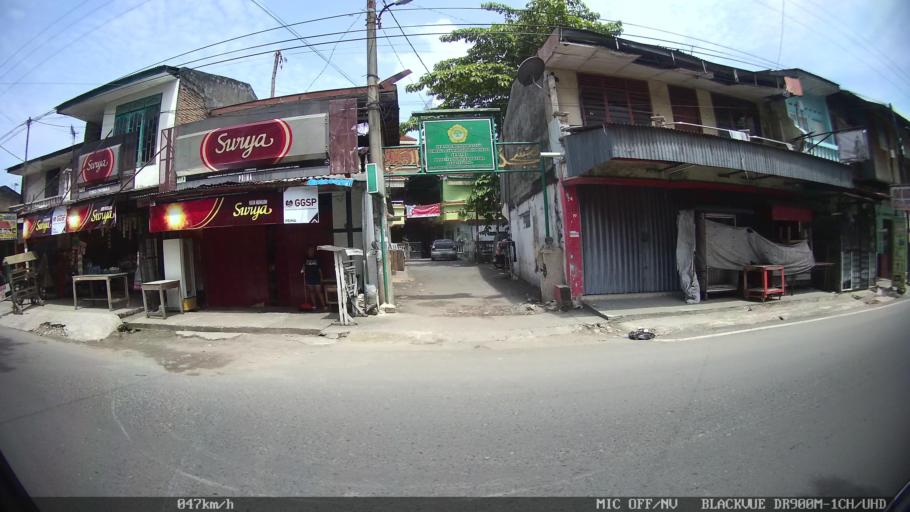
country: ID
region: North Sumatra
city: Medan
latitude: 3.5881
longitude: 98.6578
